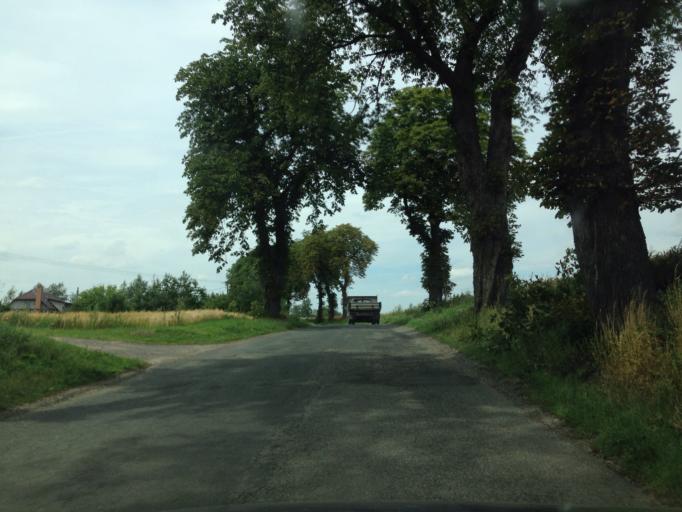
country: PL
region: Kujawsko-Pomorskie
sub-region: Powiat brodnicki
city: Brodnica
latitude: 53.2909
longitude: 19.4134
